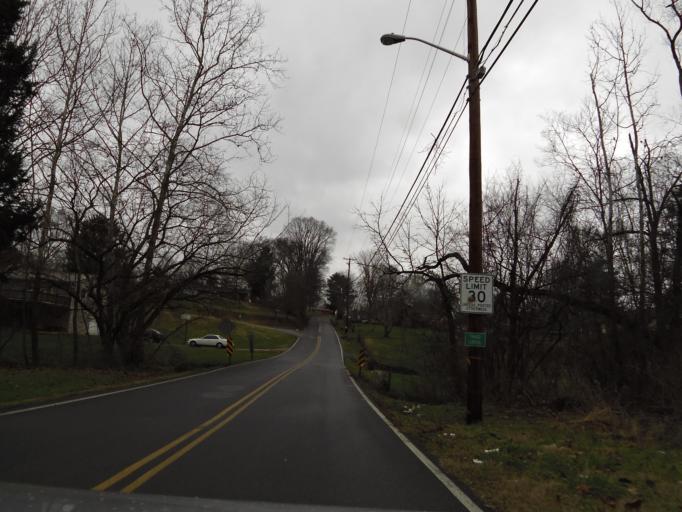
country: US
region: Tennessee
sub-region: Knox County
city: Knoxville
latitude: 35.9809
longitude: -84.0042
